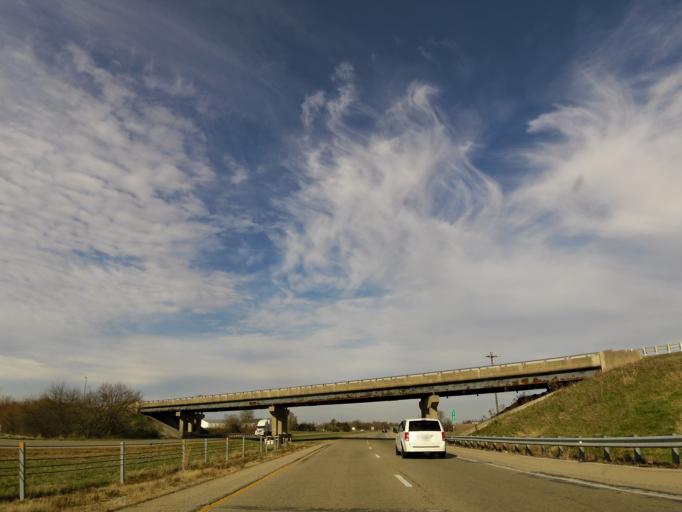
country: US
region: Illinois
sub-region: McLean County
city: Danvers
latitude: 40.5816
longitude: -89.1407
